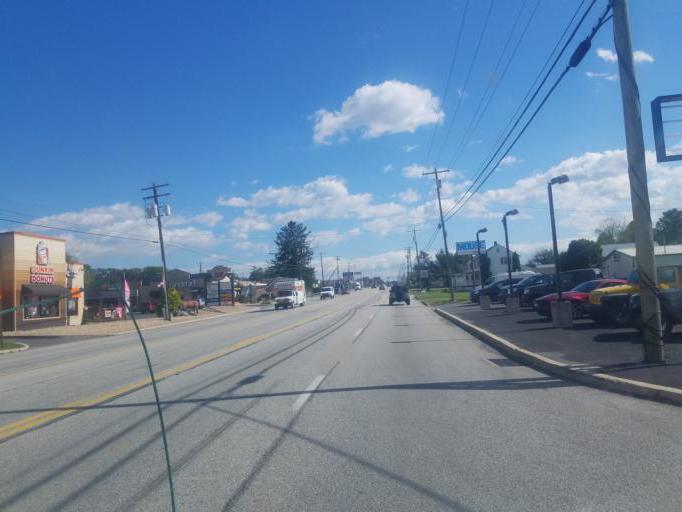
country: US
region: Pennsylvania
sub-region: Franklin County
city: Guilford
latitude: 39.9252
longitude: -77.6173
